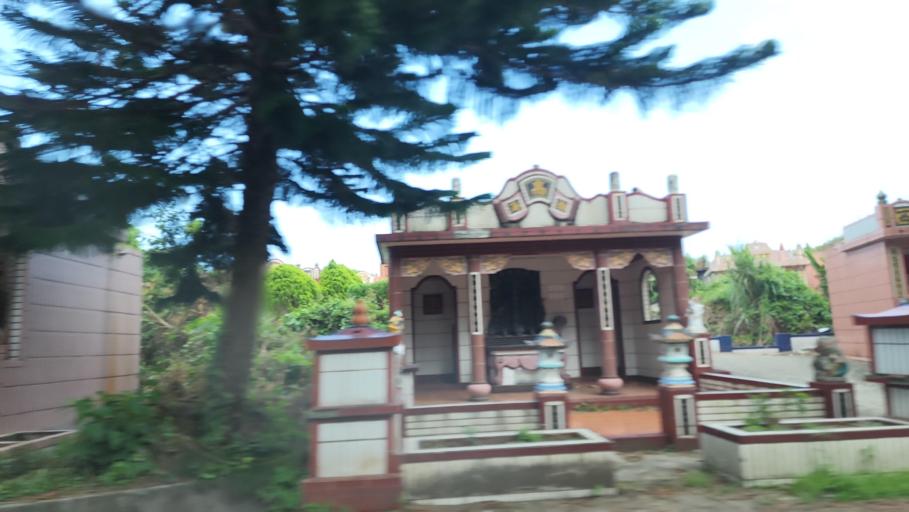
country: TW
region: Taiwan
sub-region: Keelung
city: Keelung
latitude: 25.2252
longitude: 121.6379
